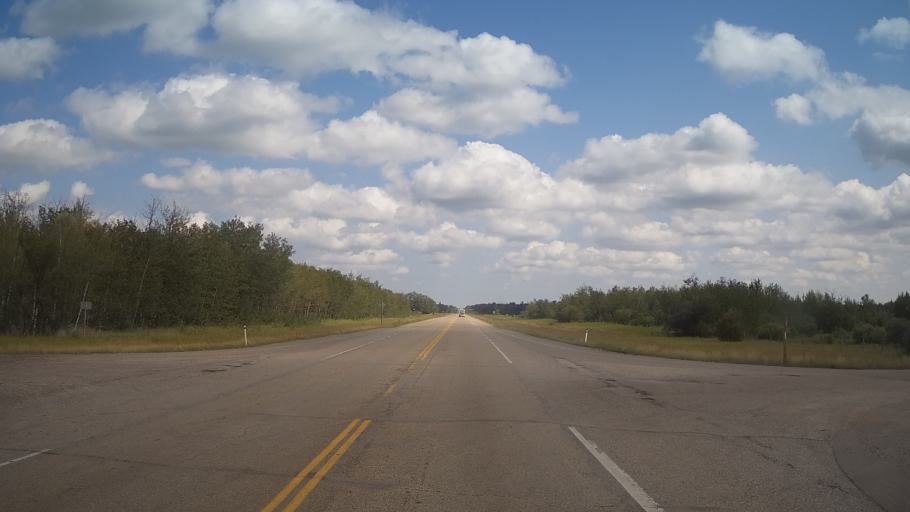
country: CA
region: Alberta
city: Sherwood Park
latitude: 53.3958
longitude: -113.0501
